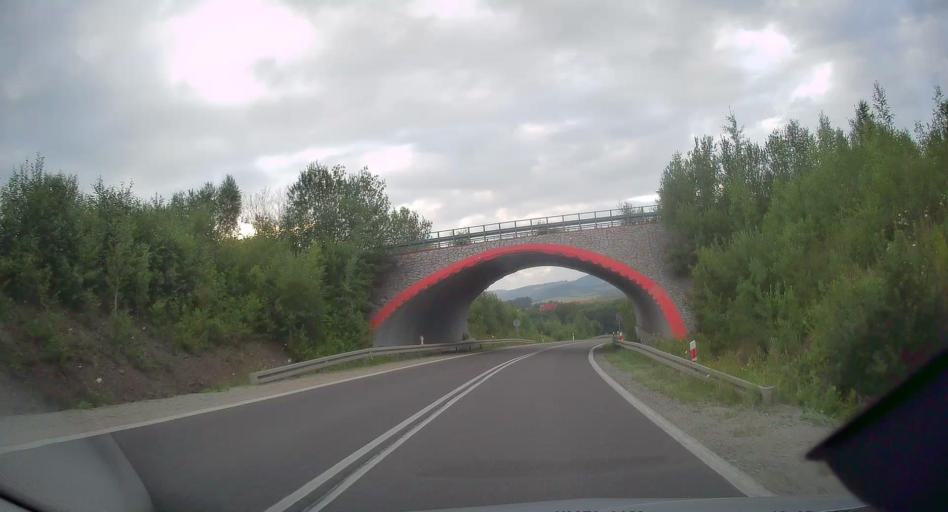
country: PL
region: Lower Silesian Voivodeship
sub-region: Powiat klodzki
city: Nowa Ruda
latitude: 50.5935
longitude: 16.5212
